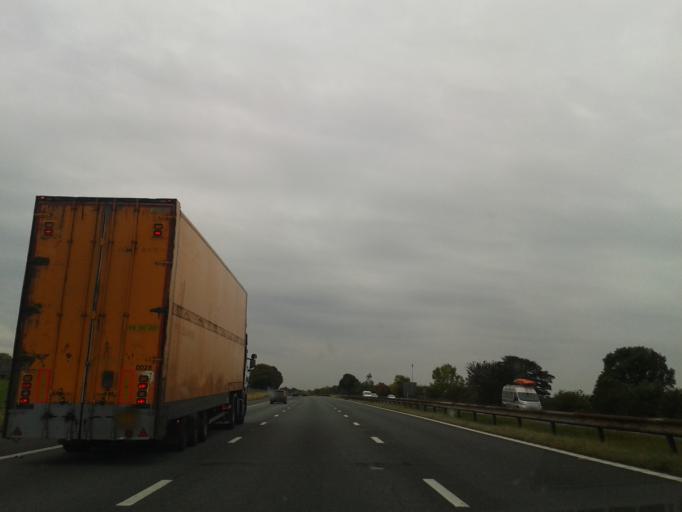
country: GB
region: England
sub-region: Cumbria
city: Milnthorpe
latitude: 54.2104
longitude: -2.7234
